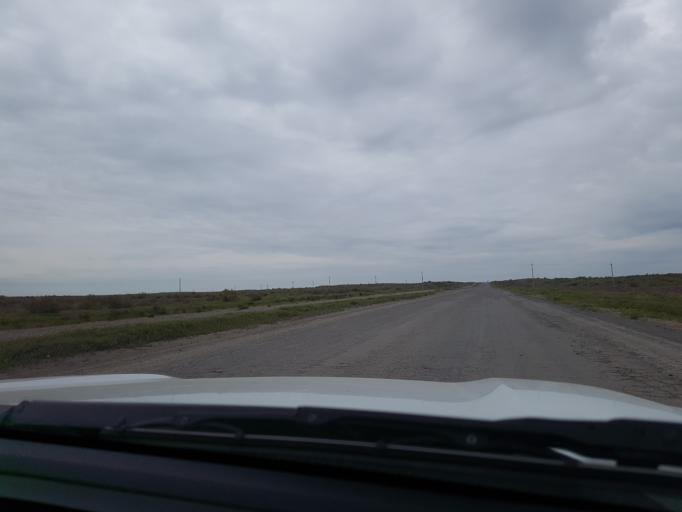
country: TM
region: Mary
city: Bayramaly
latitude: 37.9203
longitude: 62.6235
